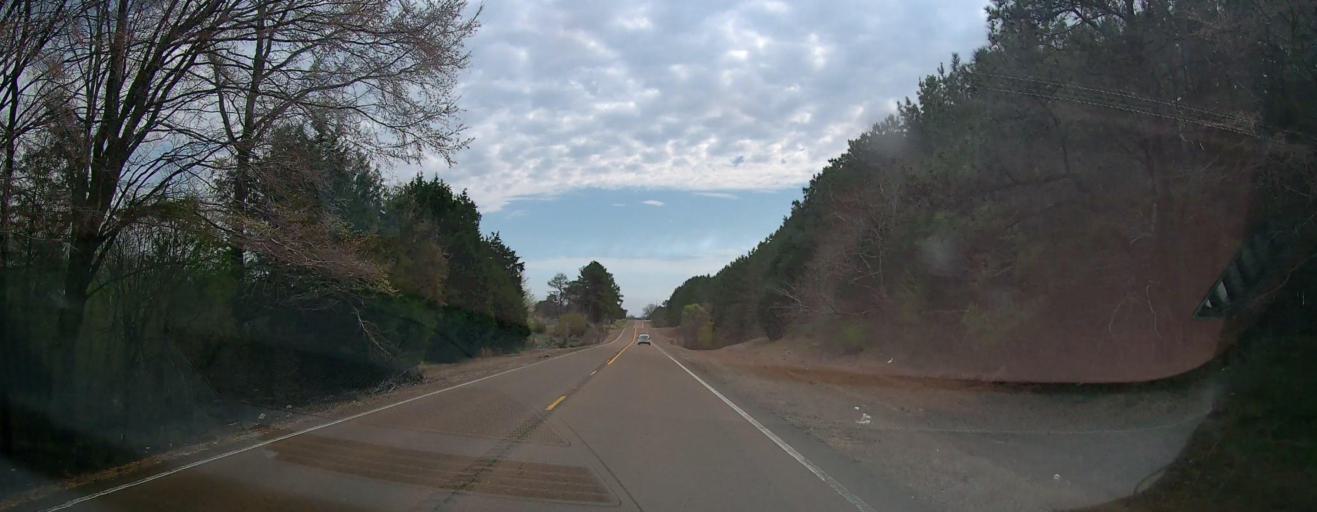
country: US
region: Mississippi
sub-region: Marshall County
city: Holly Springs
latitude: 34.8131
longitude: -89.5225
